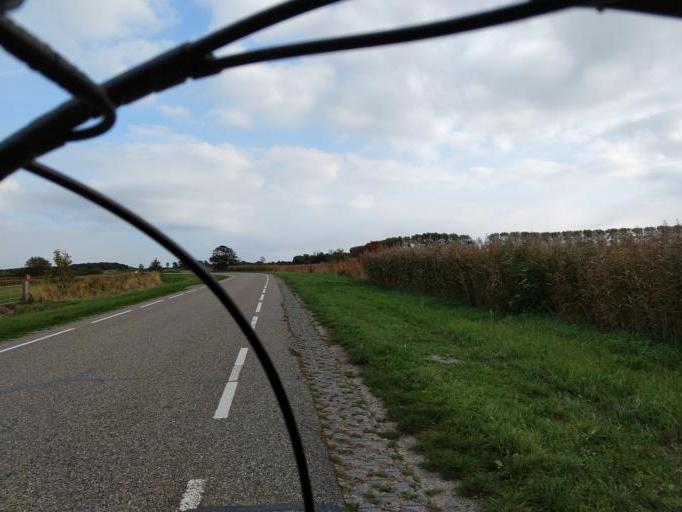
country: NL
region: Zeeland
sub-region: Schouwen-Duiveland
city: Bruinisse
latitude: 51.6807
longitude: 4.0138
